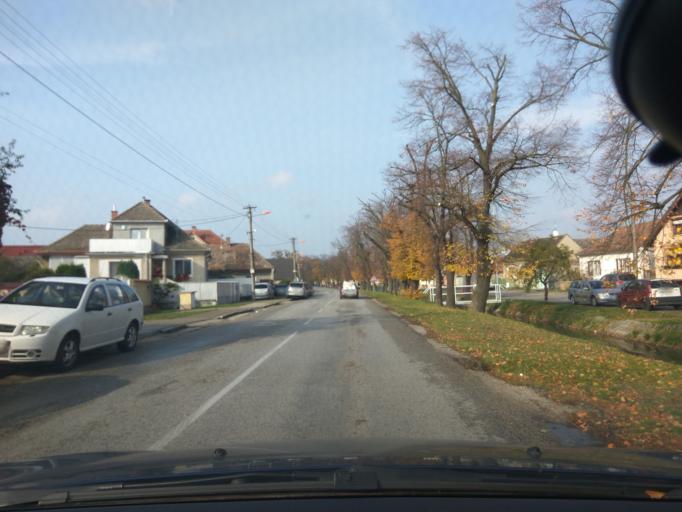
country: SK
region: Trnavsky
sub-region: Okres Trnava
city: Piestany
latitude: 48.6189
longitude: 17.7939
